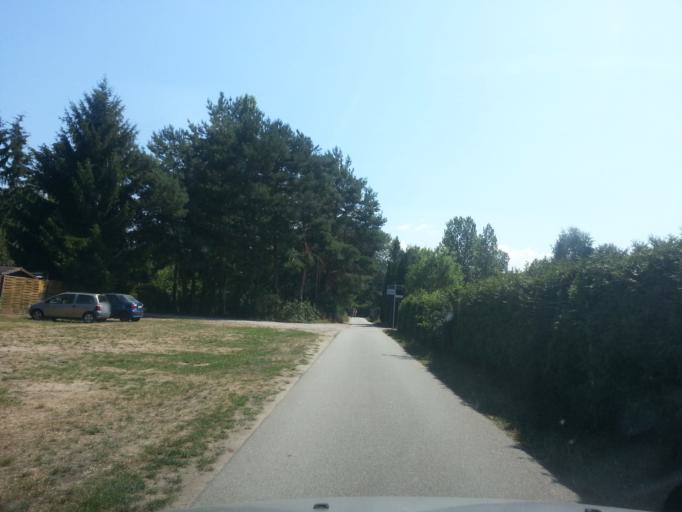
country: DE
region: Hesse
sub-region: Regierungsbezirk Darmstadt
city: Einhausen
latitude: 49.6579
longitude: 8.5465
